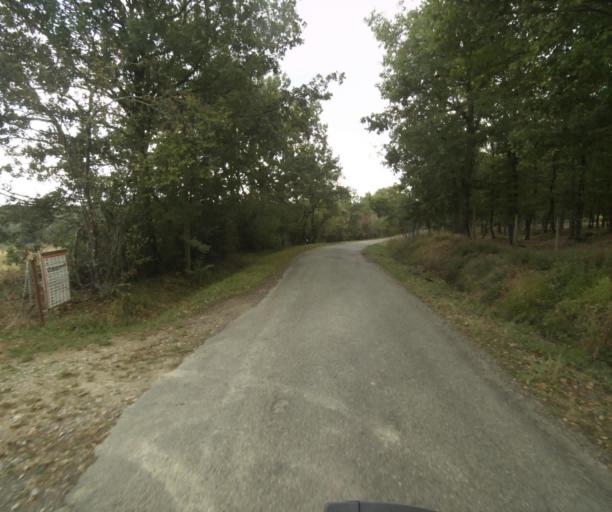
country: FR
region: Midi-Pyrenees
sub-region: Departement du Tarn-et-Garonne
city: Verdun-sur-Garonne
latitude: 43.8585
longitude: 1.1448
